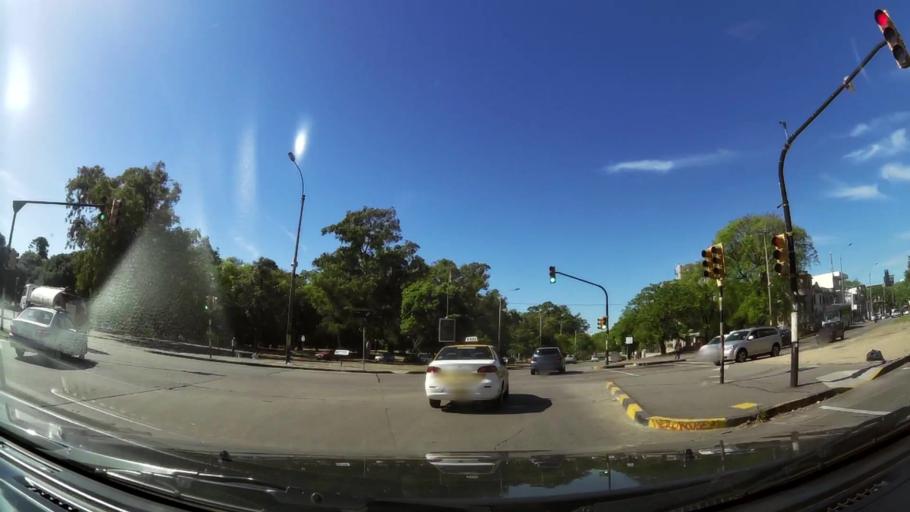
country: UY
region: Montevideo
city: Montevideo
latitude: -34.8920
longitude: -56.1589
